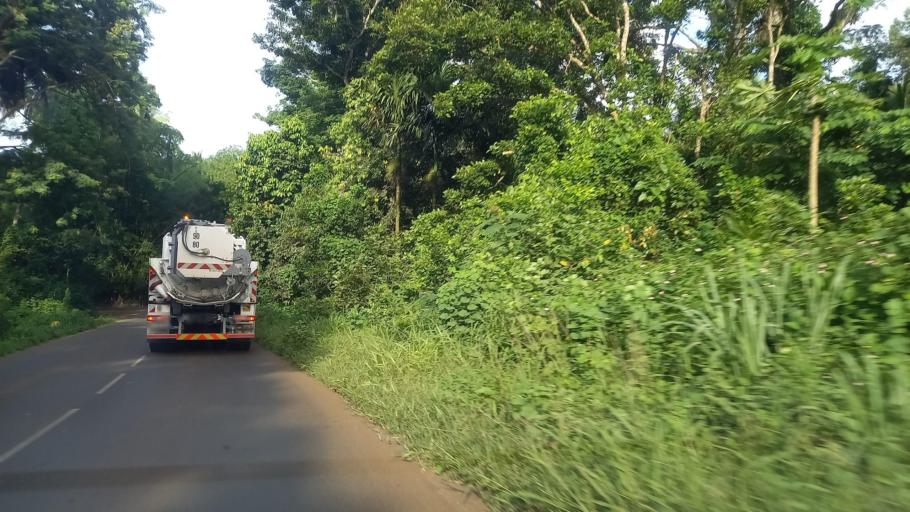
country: YT
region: Chiconi
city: Chiconi
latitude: -12.8159
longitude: 45.1289
